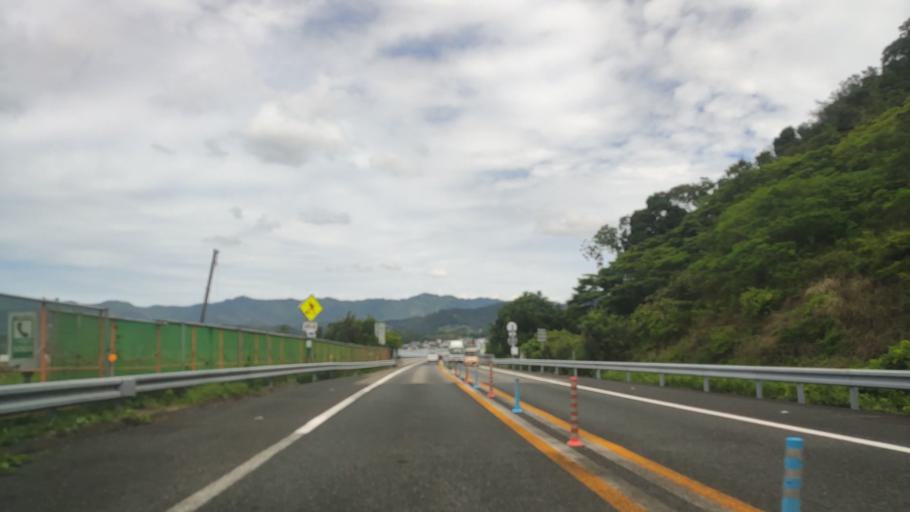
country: JP
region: Wakayama
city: Gobo
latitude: 33.8965
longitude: 135.1840
